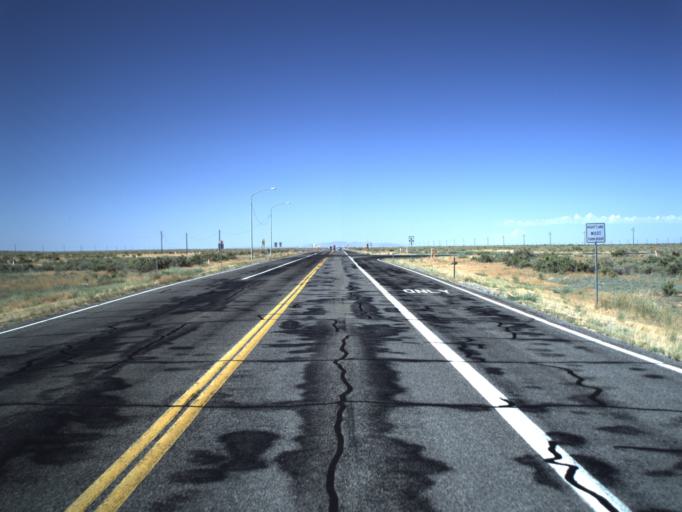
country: US
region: Utah
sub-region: Millard County
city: Delta
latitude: 39.4629
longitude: -112.4320
